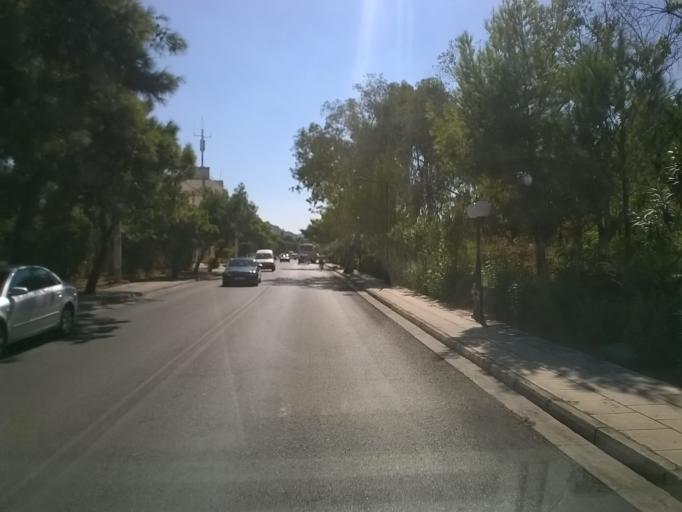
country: GR
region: Attica
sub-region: Nomarchia Anatolikis Attikis
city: Voula
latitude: 37.8423
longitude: 23.7641
